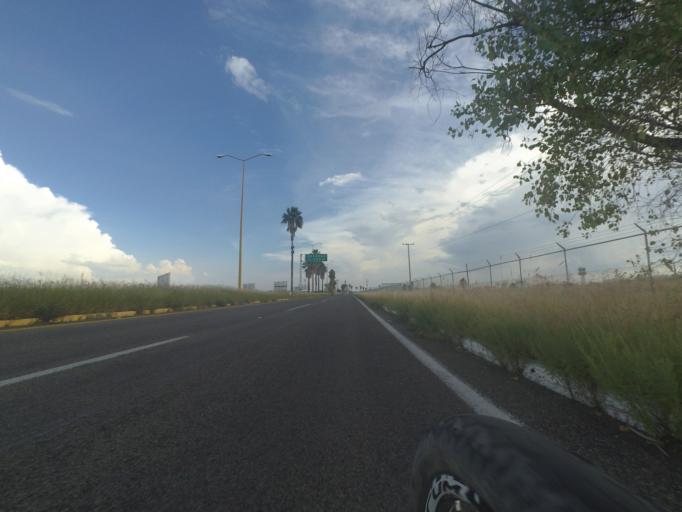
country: MX
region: Aguascalientes
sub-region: Aguascalientes
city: Penuelas (El Cienegal)
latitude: 21.7063
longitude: -102.3110
